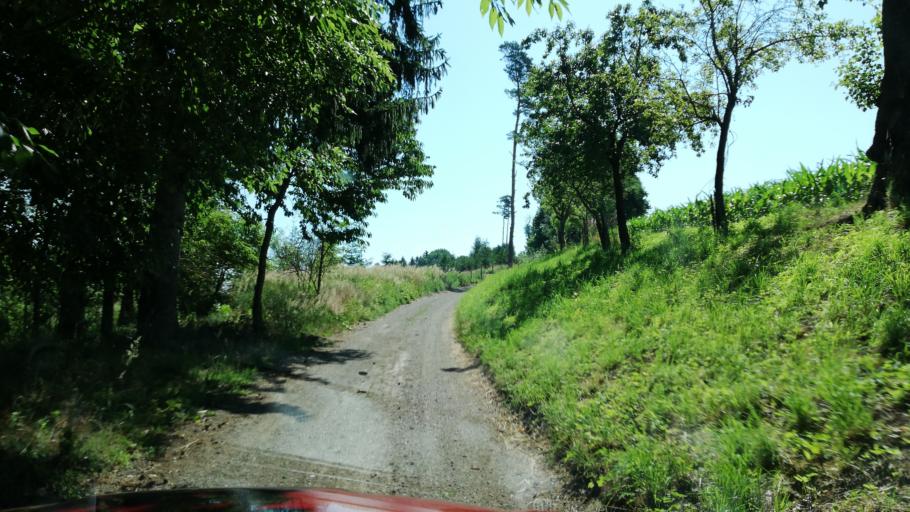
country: AT
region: Upper Austria
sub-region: Wels-Land
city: Gunskirchen
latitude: 48.1815
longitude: 13.9347
